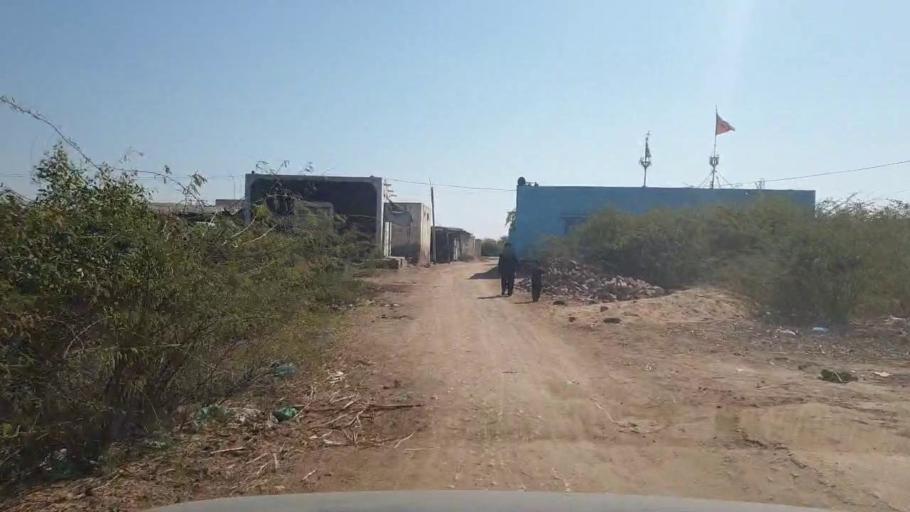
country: PK
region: Sindh
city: Mirwah Gorchani
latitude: 25.2901
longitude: 69.1271
